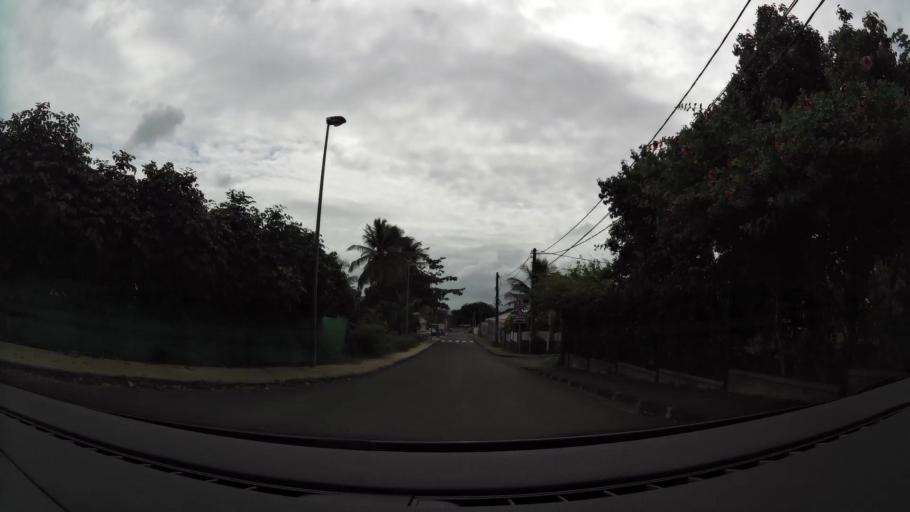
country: GP
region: Guadeloupe
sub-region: Guadeloupe
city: Baie-Mahault
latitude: 16.2549
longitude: -61.5800
